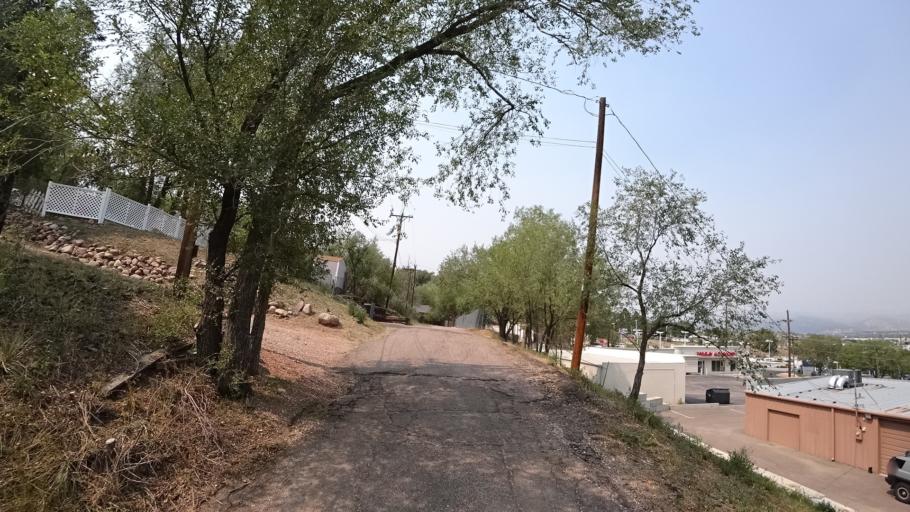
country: US
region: Colorado
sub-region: El Paso County
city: Colorado Springs
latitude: 38.8131
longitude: -104.8299
